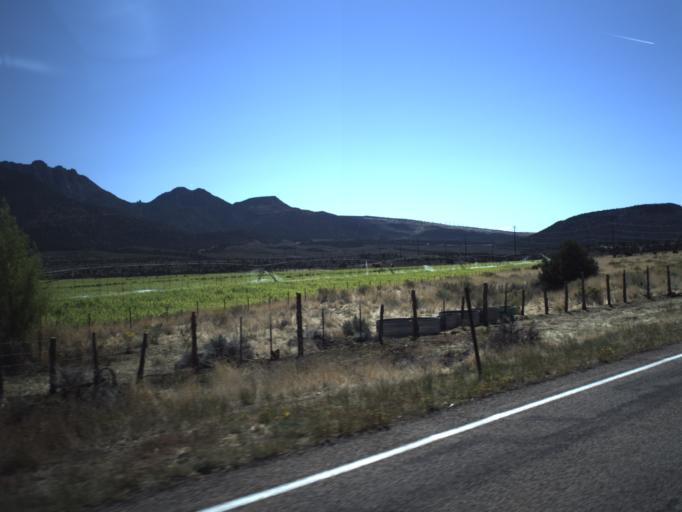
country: US
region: Utah
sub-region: Washington County
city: Enterprise
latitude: 37.4099
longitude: -113.6339
